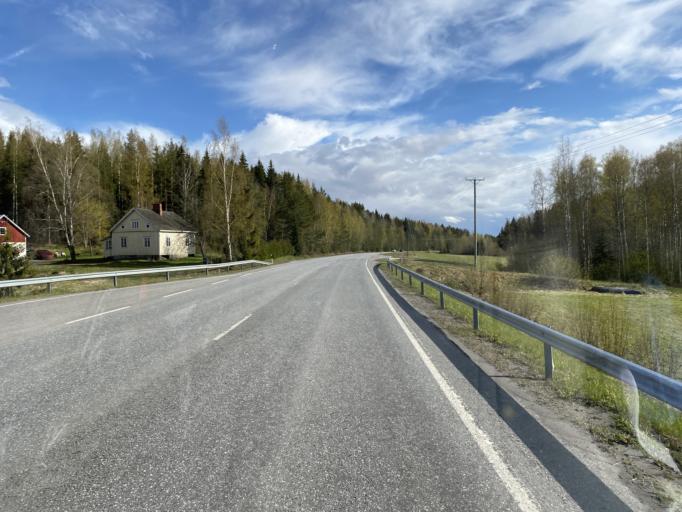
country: FI
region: Pirkanmaa
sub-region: Etelae-Pirkanmaa
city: Viiala
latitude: 61.2568
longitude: 23.7438
